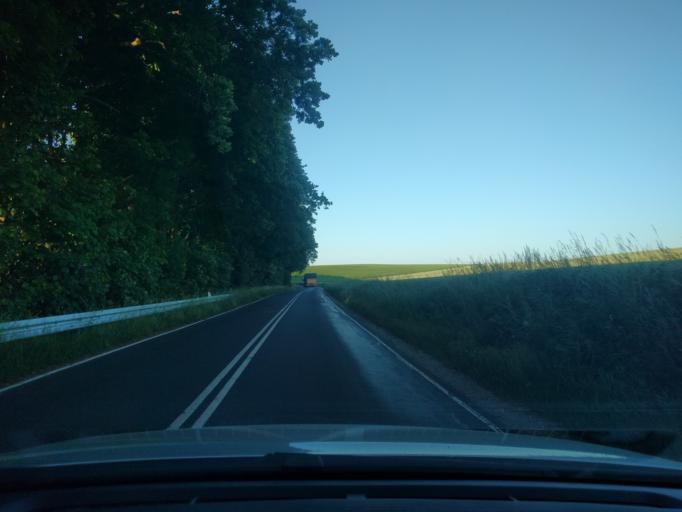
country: DK
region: South Denmark
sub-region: Kerteminde Kommune
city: Kerteminde
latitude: 55.5351
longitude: 10.6580
